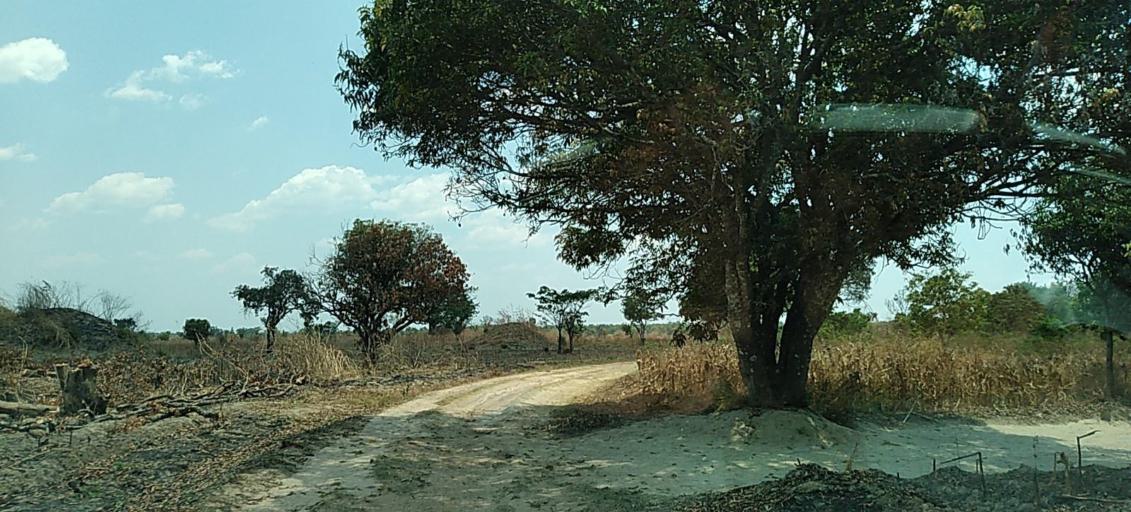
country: ZM
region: Copperbelt
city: Chililabombwe
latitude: -12.4889
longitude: 27.6662
